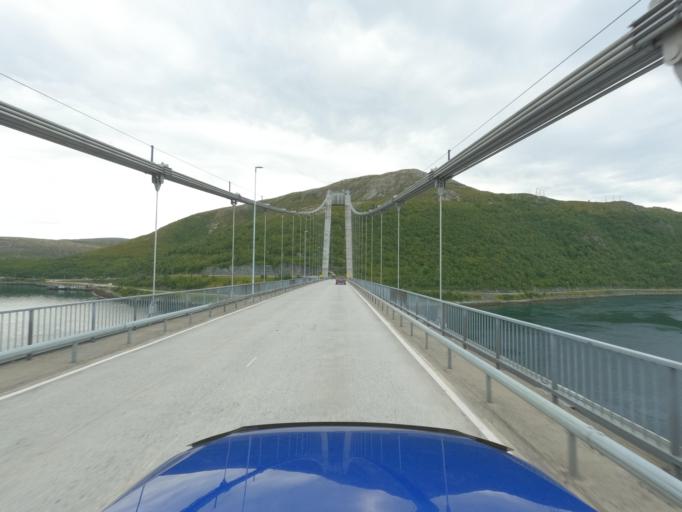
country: NO
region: Finnmark Fylke
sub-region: Kvalsund
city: Kvalsund
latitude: 70.5119
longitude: 23.9519
